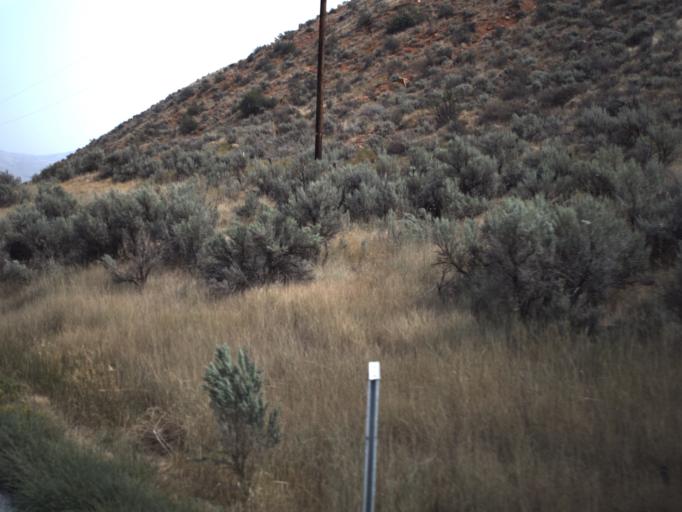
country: US
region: Utah
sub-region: Summit County
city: Coalville
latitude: 41.0107
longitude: -111.5165
